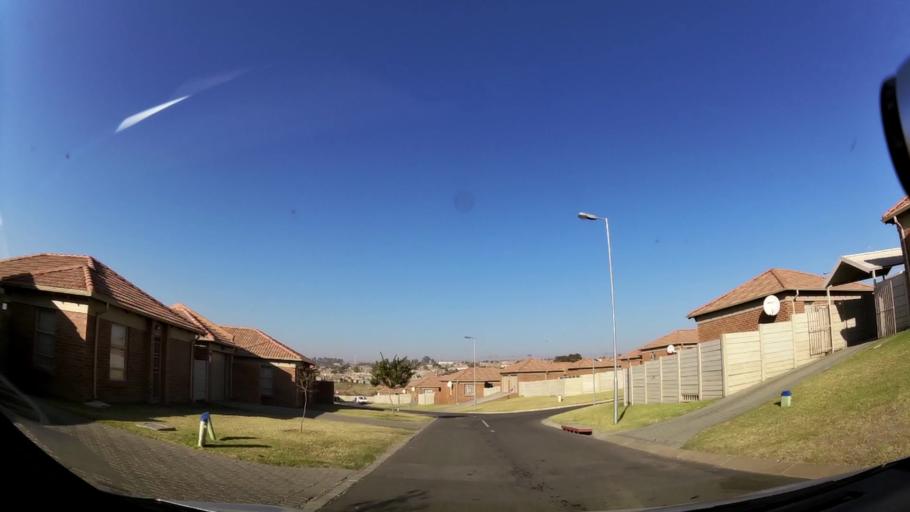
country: ZA
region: Gauteng
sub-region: City of Johannesburg Metropolitan Municipality
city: Midrand
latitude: -25.9094
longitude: 28.1146
